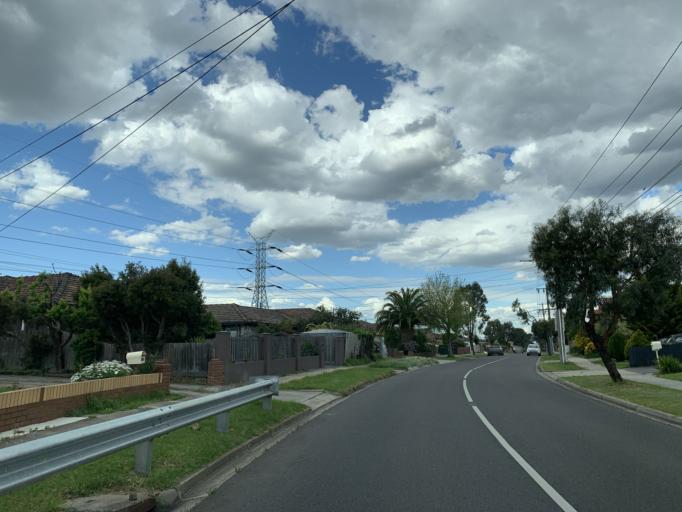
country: AU
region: Victoria
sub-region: Moonee Valley
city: Keilor East
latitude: -37.7408
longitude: 144.8536
